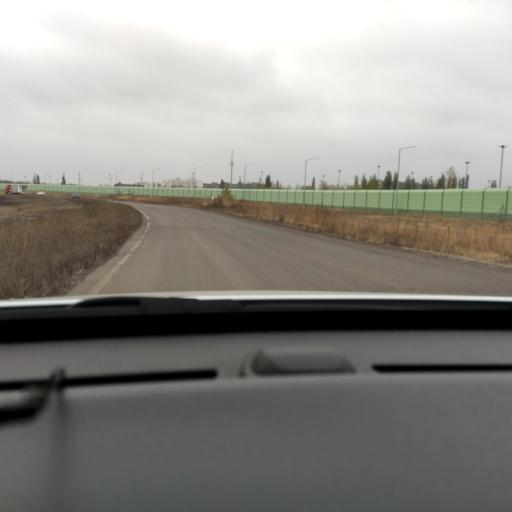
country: RU
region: Voronezj
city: Novaya Usman'
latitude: 51.6520
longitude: 39.3042
